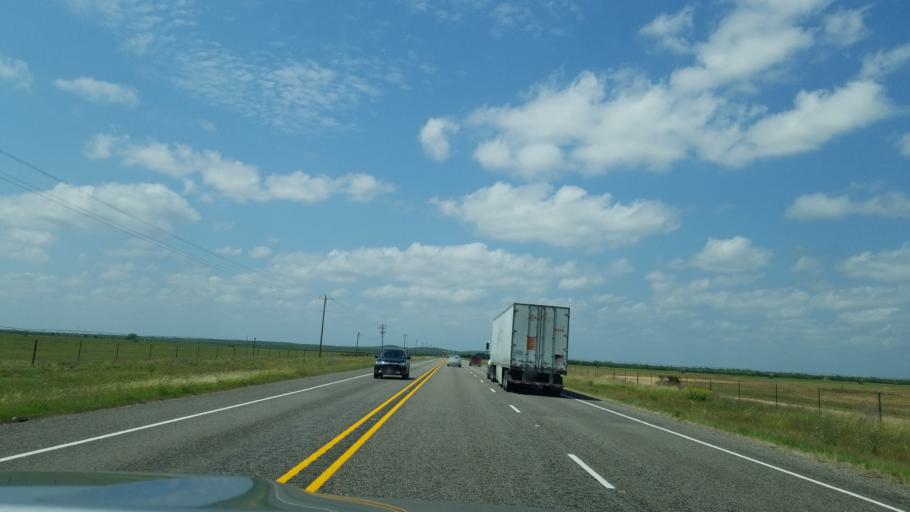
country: US
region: Texas
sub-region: Frio County
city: Pearsall
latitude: 28.9665
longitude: -99.2495
